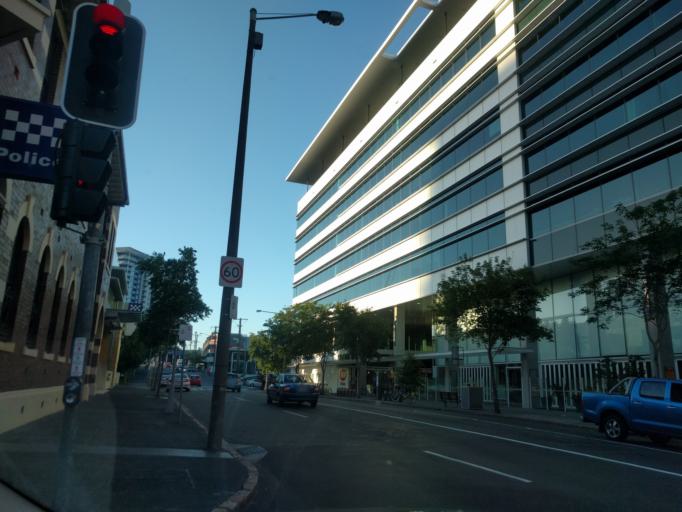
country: AU
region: Queensland
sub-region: Brisbane
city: Fortitude Valley
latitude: -27.4534
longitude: 153.0378
